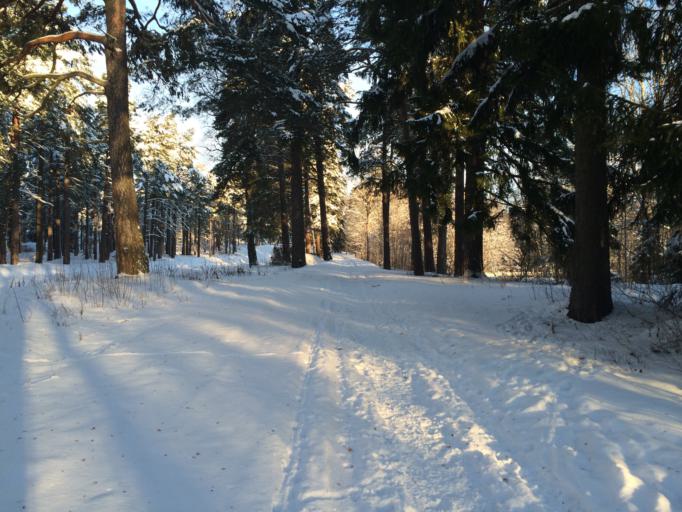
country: SE
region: Vaestmanland
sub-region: Hallstahammars Kommun
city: Hallstahammar
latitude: 59.6215
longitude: 16.2063
